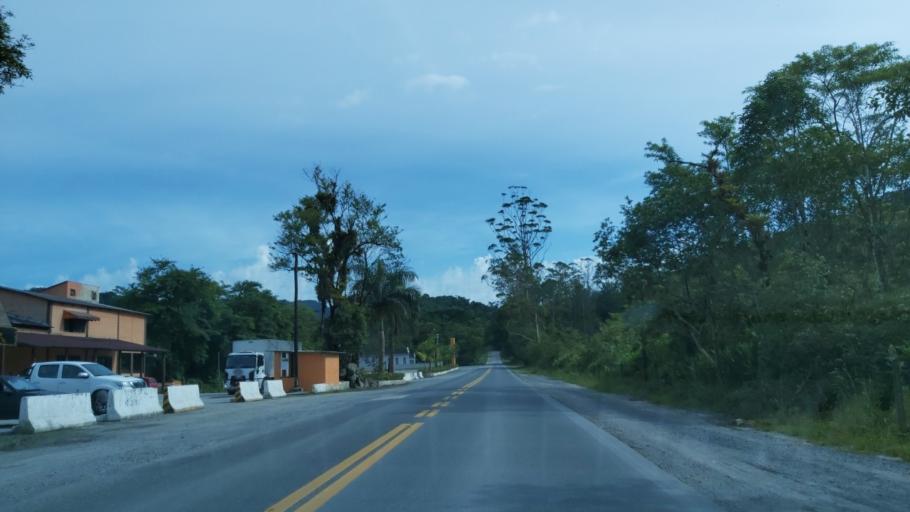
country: BR
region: Sao Paulo
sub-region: Miracatu
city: Miracatu
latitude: -24.0616
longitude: -47.5897
